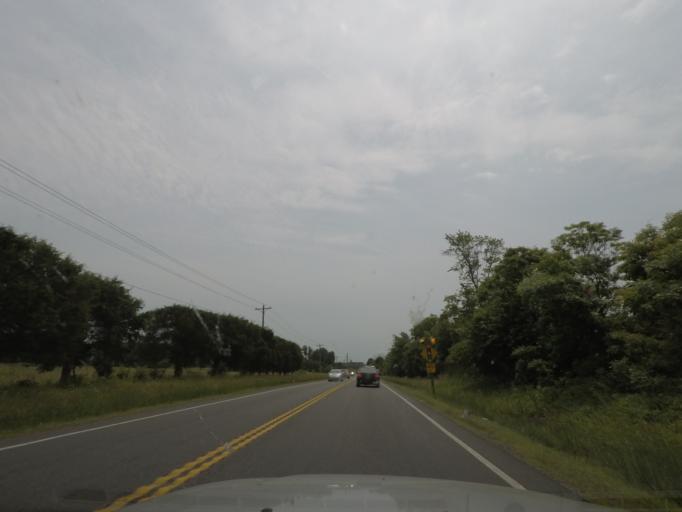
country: US
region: Virginia
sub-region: Prince William County
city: Bull Run Mountain Estates
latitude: 38.9031
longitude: -77.6299
